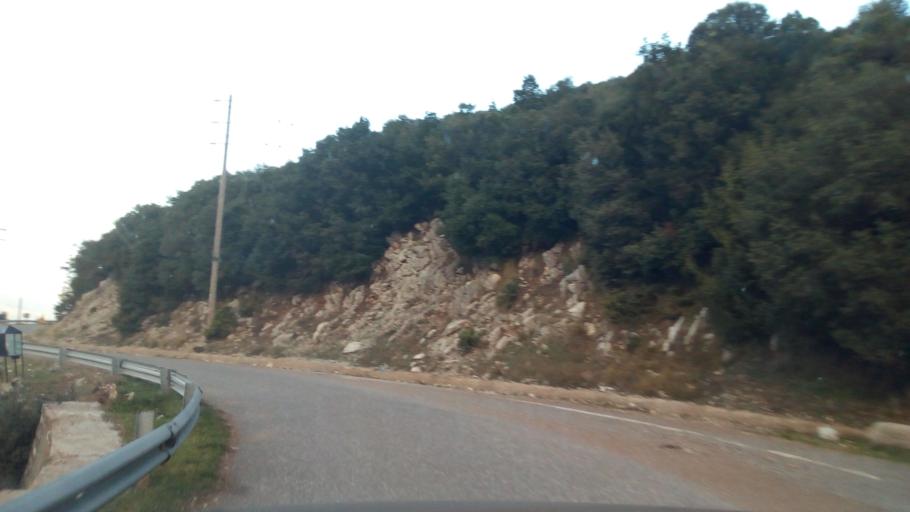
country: GR
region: West Greece
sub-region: Nomos Aitolias kai Akarnanias
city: Nafpaktos
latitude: 38.5214
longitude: 21.8413
